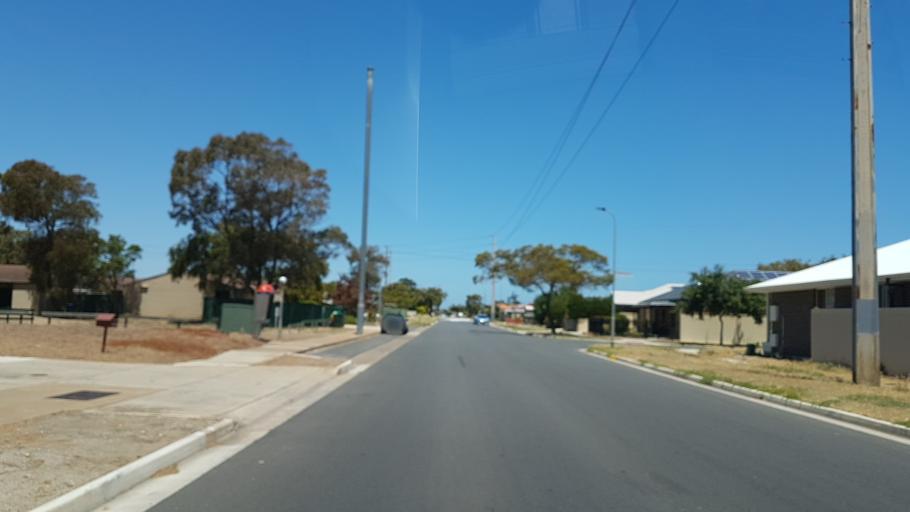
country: AU
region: South Australia
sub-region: Charles Sturt
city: West Lakes Shore
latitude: -34.8552
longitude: 138.4882
